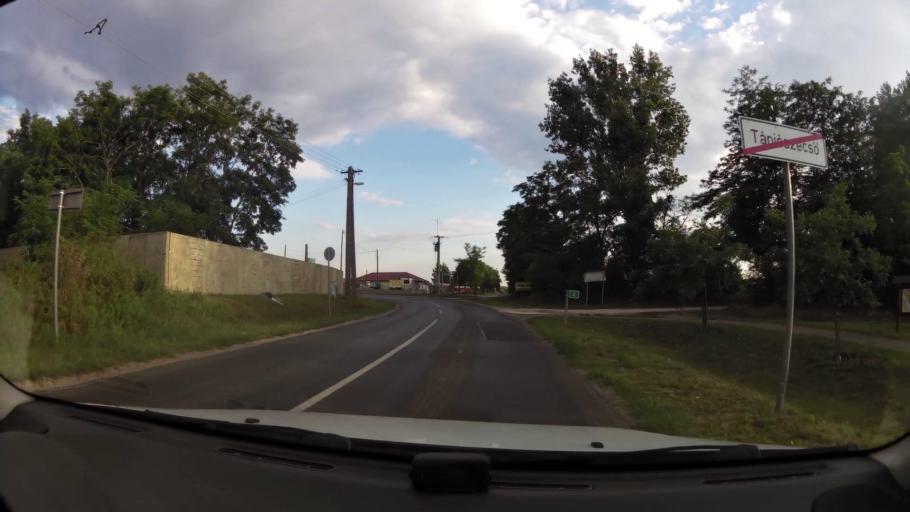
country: HU
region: Pest
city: Tapioszecso
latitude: 47.4381
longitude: 19.5954
